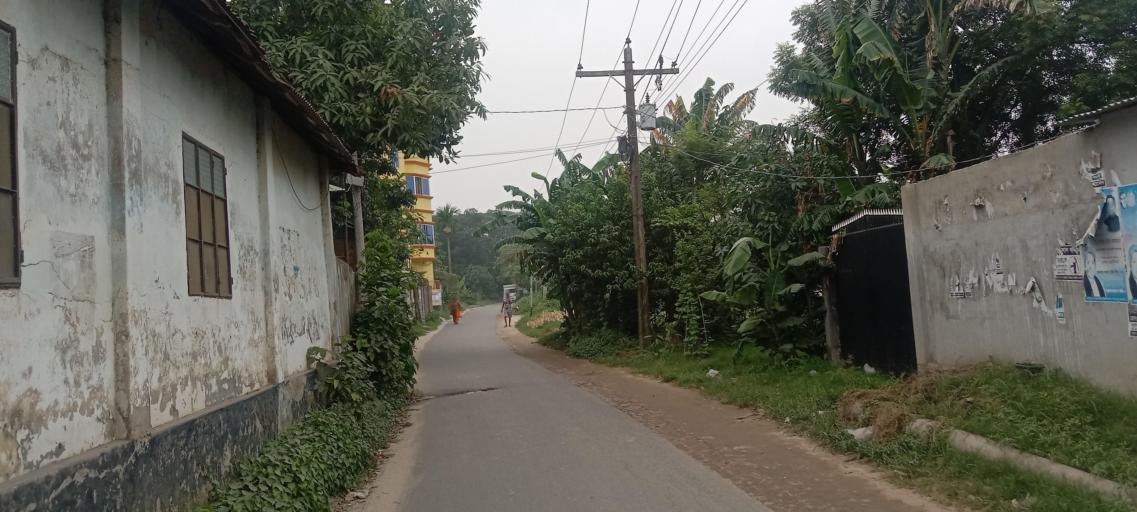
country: BD
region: Dhaka
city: Azimpur
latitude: 23.7349
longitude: 90.3223
